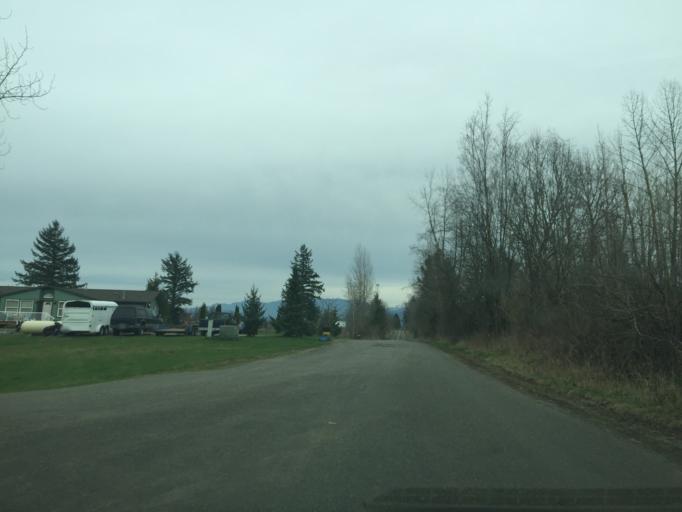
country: US
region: Washington
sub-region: Whatcom County
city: Everson
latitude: 48.9493
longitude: -122.3762
